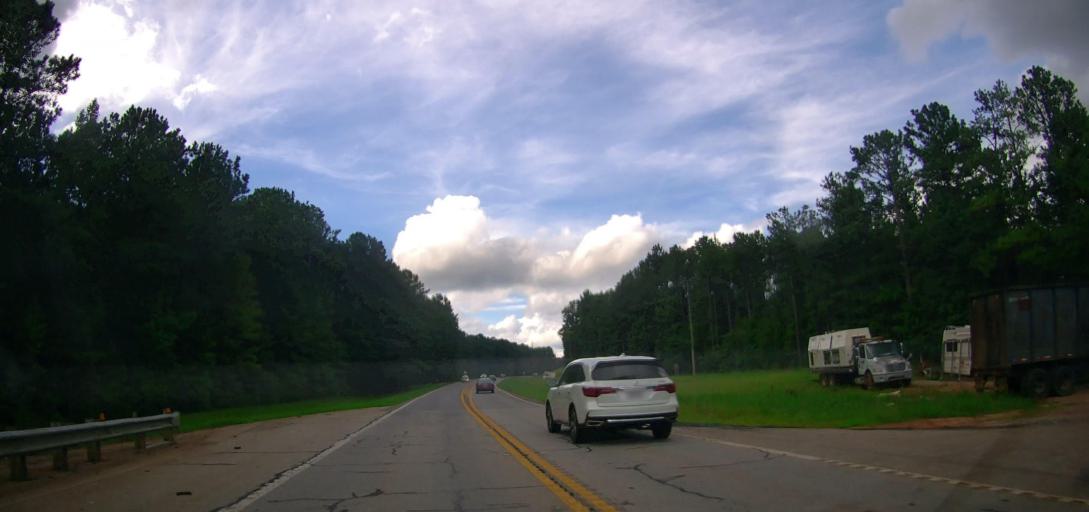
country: US
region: Georgia
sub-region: Harris County
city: Hamilton
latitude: 32.7094
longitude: -84.8705
